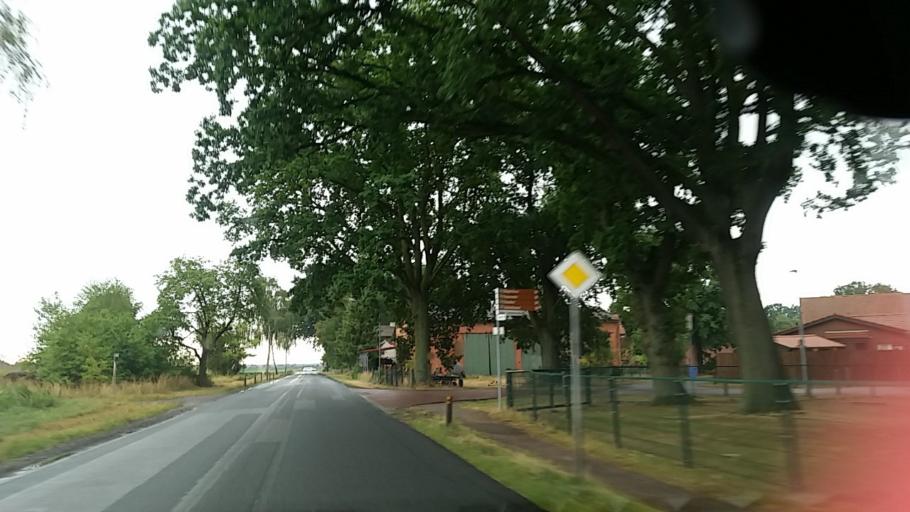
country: DE
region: Lower Saxony
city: Sassenburg
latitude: 52.5565
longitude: 10.6777
